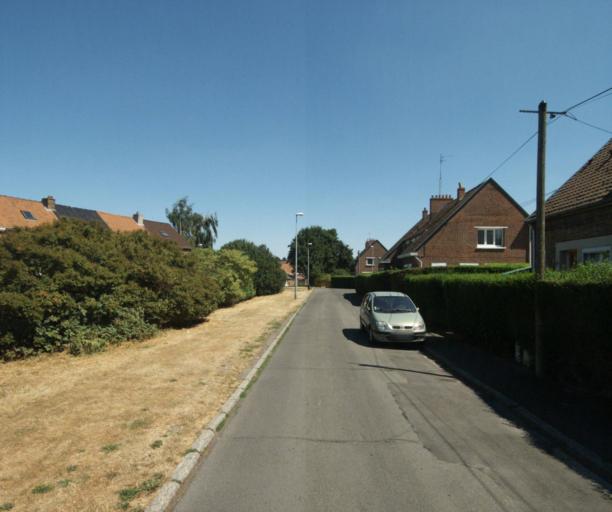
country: BE
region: Wallonia
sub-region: Province du Hainaut
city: Mouscron
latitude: 50.7394
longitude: 3.1907
